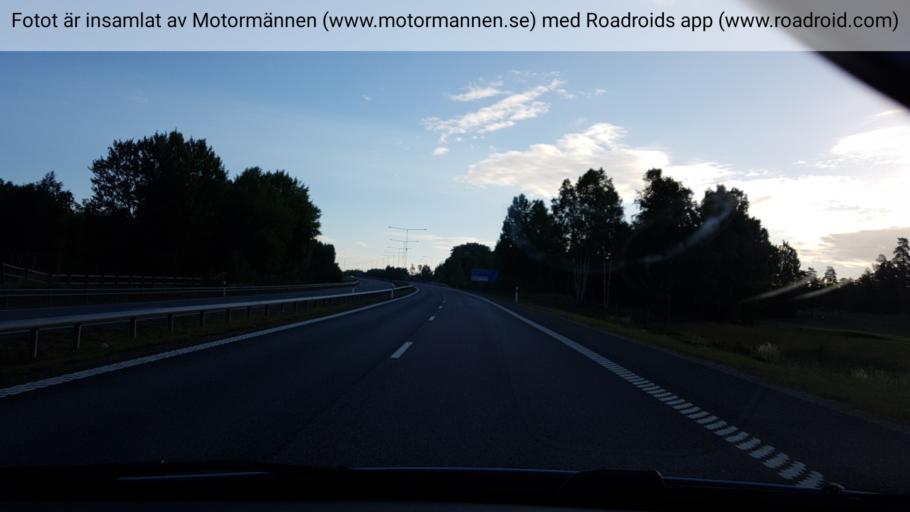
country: SE
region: Stockholm
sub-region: Haninge Kommun
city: Jordbro
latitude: 59.1019
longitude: 18.1195
